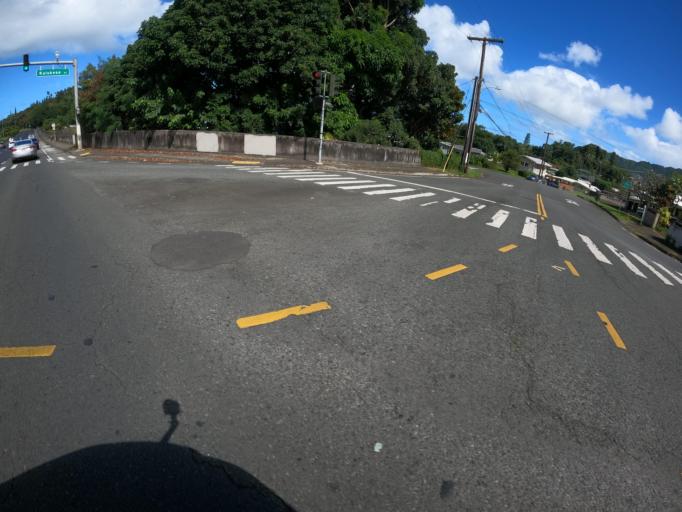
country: US
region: Hawaii
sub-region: Honolulu County
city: Kane'ohe
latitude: 21.4063
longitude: -157.8070
